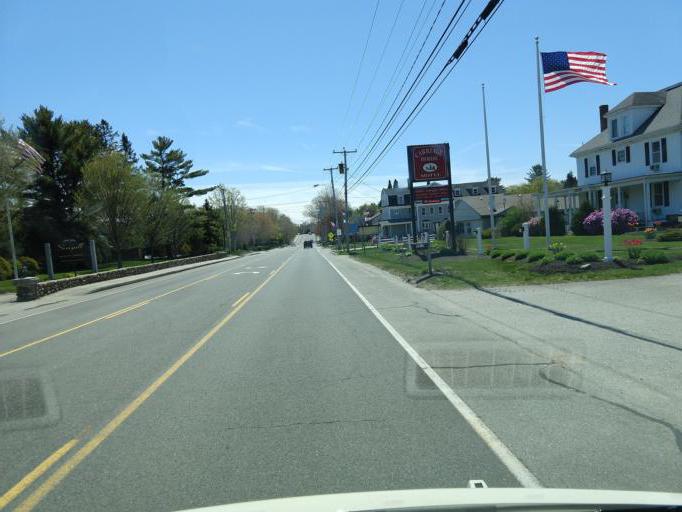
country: US
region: Maine
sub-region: York County
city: Wells Beach Station
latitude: 43.3175
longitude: -70.5831
